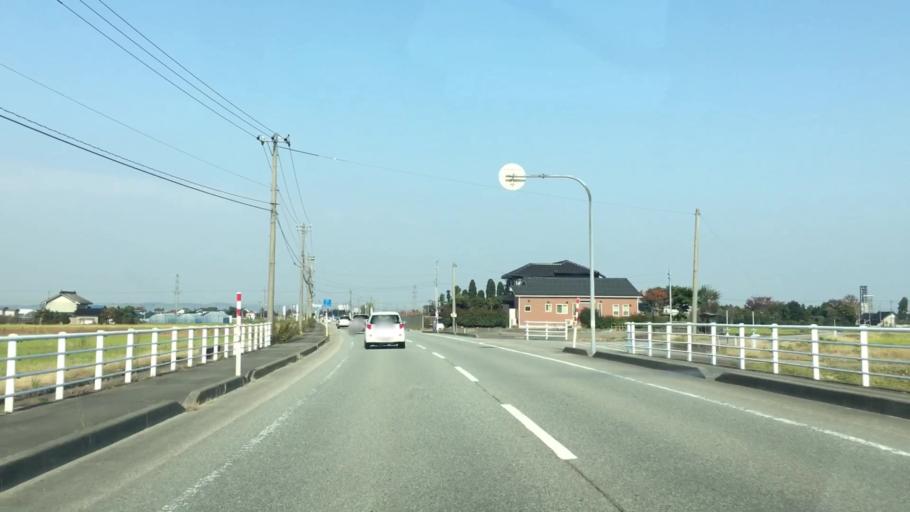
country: JP
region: Toyama
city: Yatsuomachi-higashikumisaka
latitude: 36.6096
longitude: 137.1924
